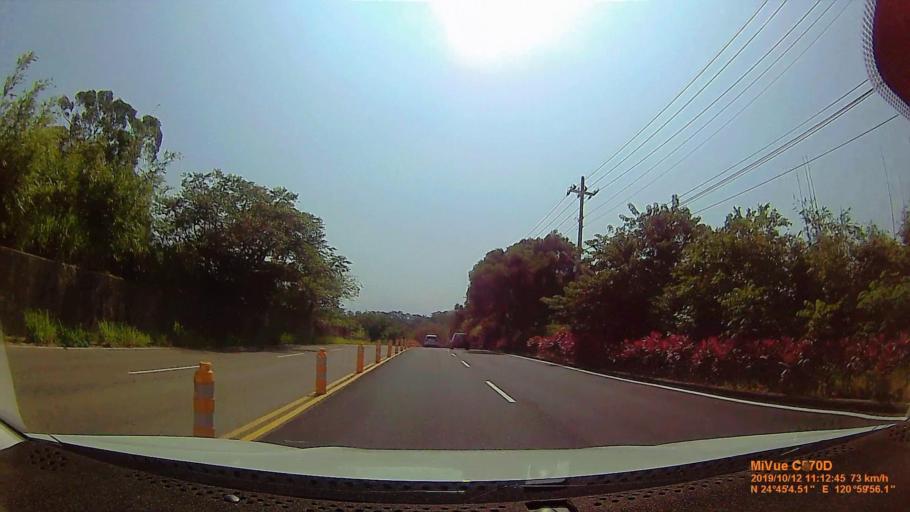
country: TW
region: Taiwan
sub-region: Hsinchu
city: Hsinchu
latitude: 24.7511
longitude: 120.9991
